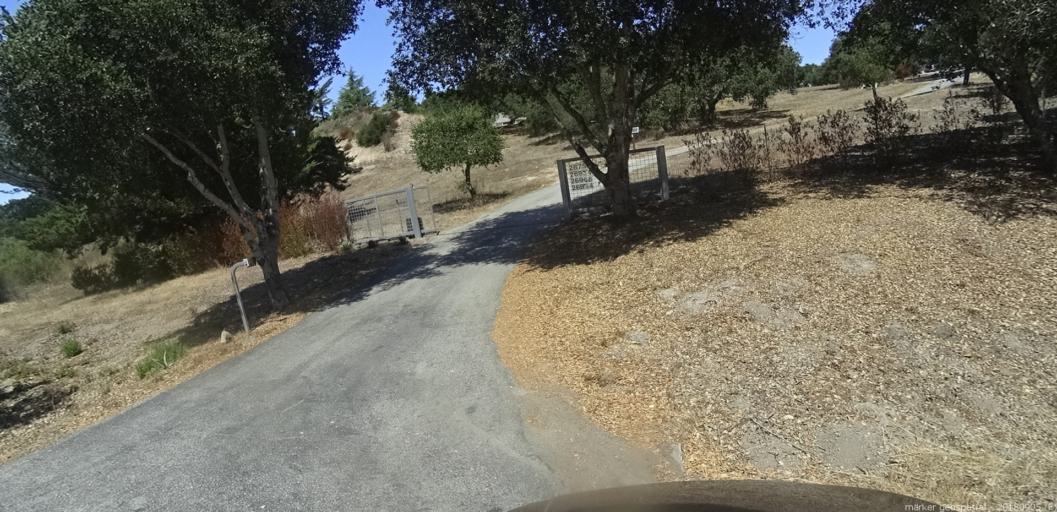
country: US
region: California
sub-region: Monterey County
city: Carmel Valley Village
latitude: 36.5384
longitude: -121.7524
